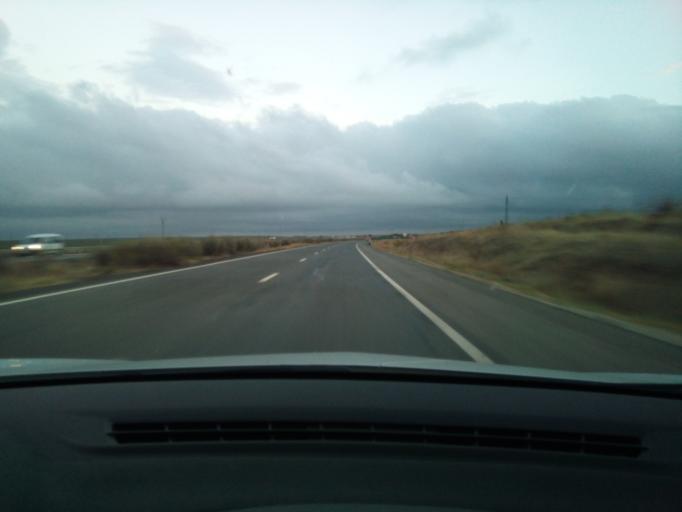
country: MA
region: Meknes-Tafilalet
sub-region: Meknes
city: Meknes
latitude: 33.8654
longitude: -5.6378
